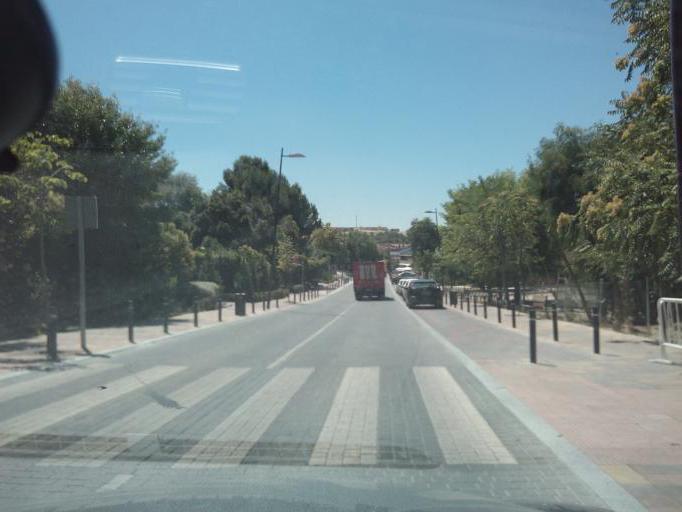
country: ES
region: Madrid
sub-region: Provincia de Madrid
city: Cobena
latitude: 40.5706
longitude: -3.5035
